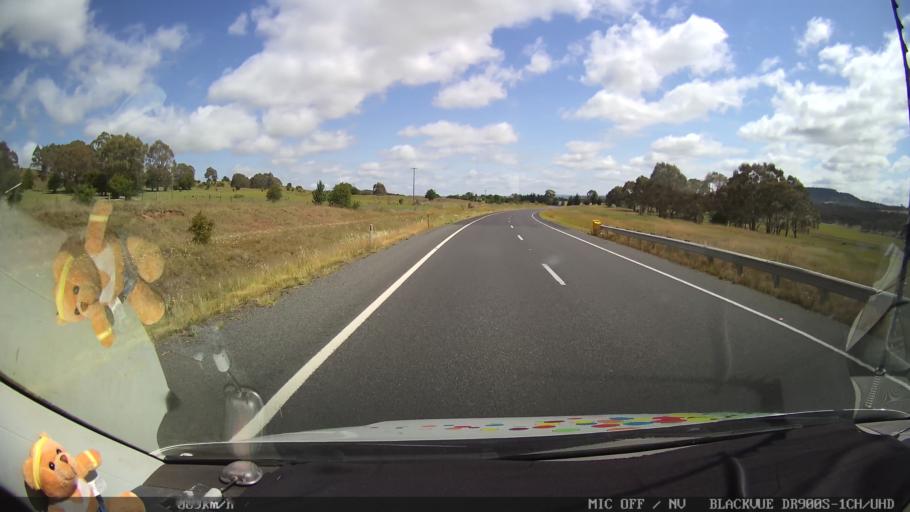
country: AU
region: New South Wales
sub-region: Glen Innes Severn
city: Glen Innes
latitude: -29.8887
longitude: 151.7332
